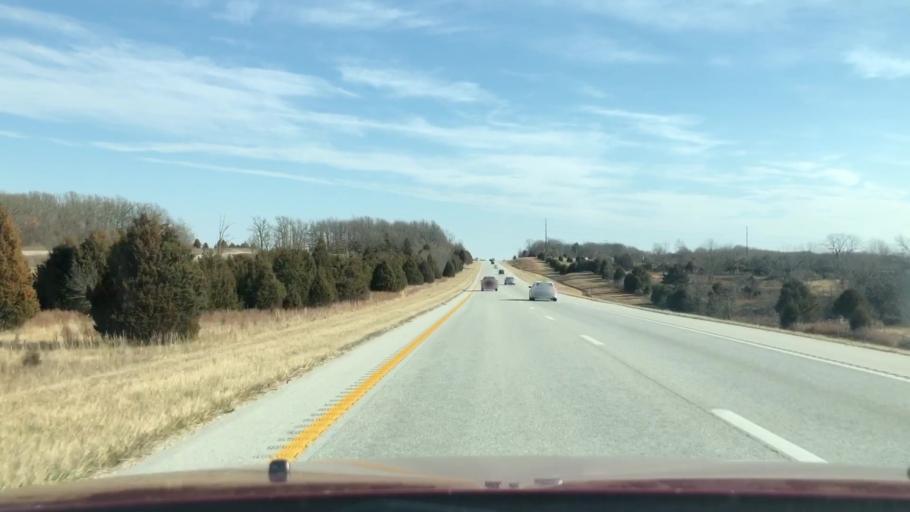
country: US
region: Missouri
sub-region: Webster County
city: Rogersville
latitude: 37.1198
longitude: -93.0098
